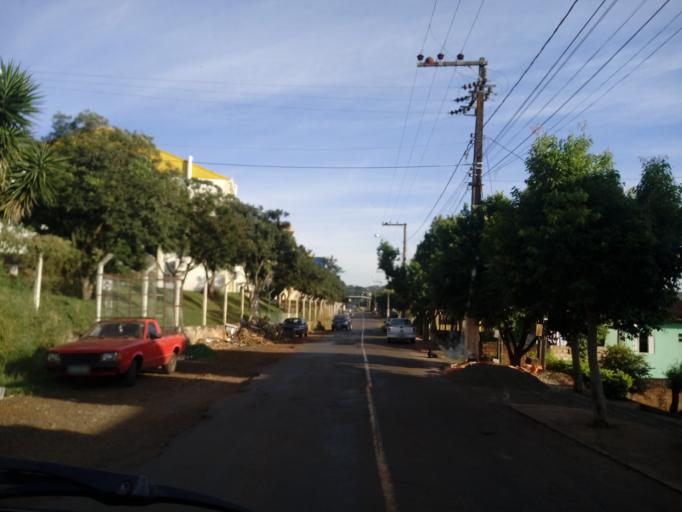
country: BR
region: Santa Catarina
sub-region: Chapeco
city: Chapeco
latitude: -27.0927
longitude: -52.6640
